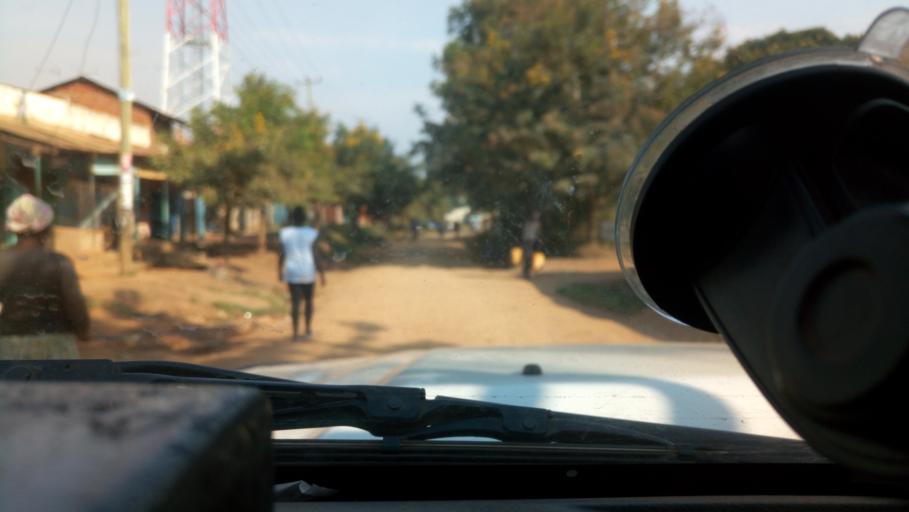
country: KE
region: Migori
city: Migori
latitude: -1.0628
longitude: 34.4719
